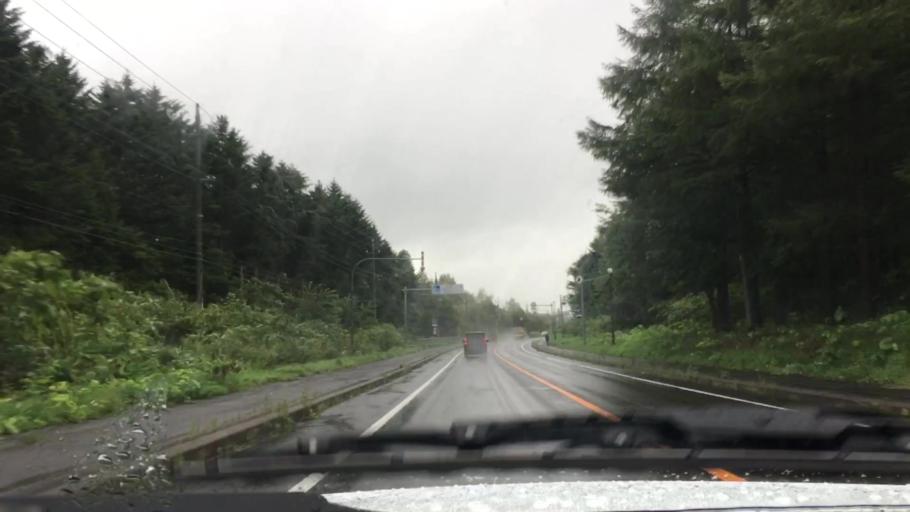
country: JP
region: Hokkaido
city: Niseko Town
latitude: 42.7455
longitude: 140.8956
